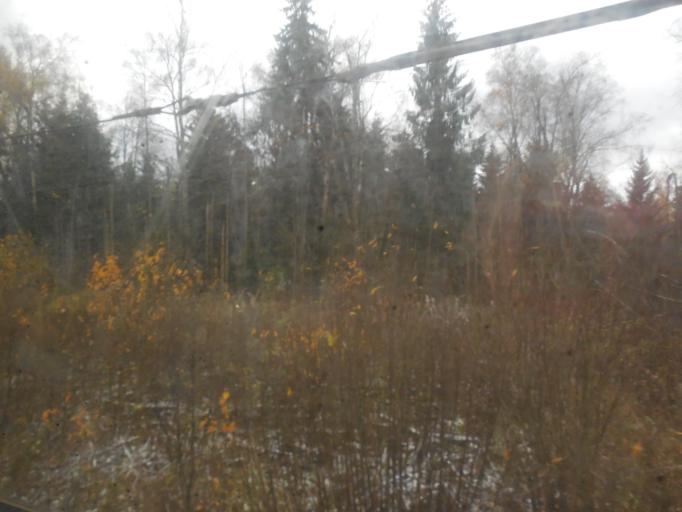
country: RU
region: Moskovskaya
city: Zvenigorod
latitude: 55.6903
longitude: 36.8728
